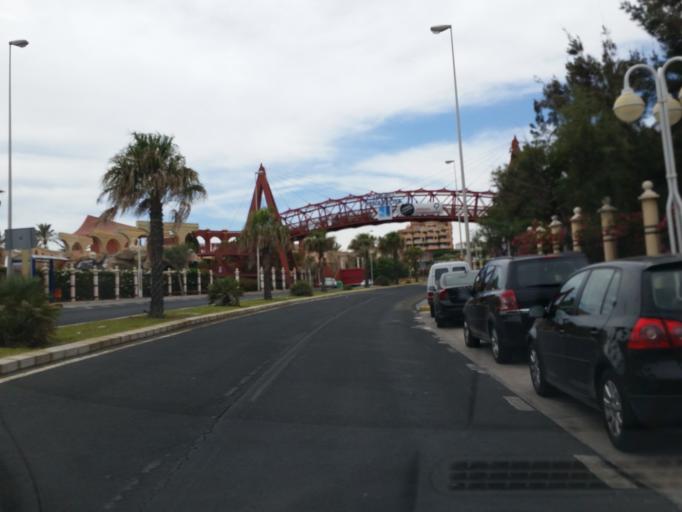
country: ES
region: Andalusia
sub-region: Provincia de Malaga
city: Benalmadena
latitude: 36.5752
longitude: -4.5800
